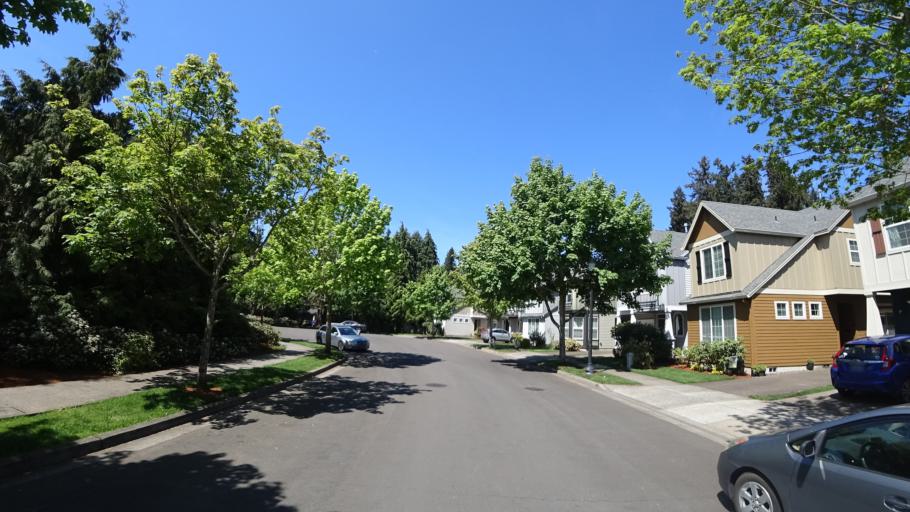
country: US
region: Oregon
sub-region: Washington County
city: Hillsboro
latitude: 45.5122
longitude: -122.9759
